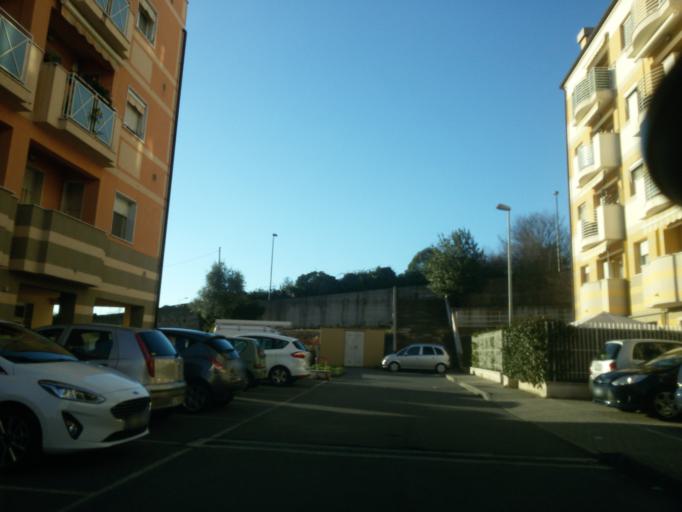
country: IT
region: Liguria
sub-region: Provincia di Savona
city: Valleggia
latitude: 44.2939
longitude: 8.4508
